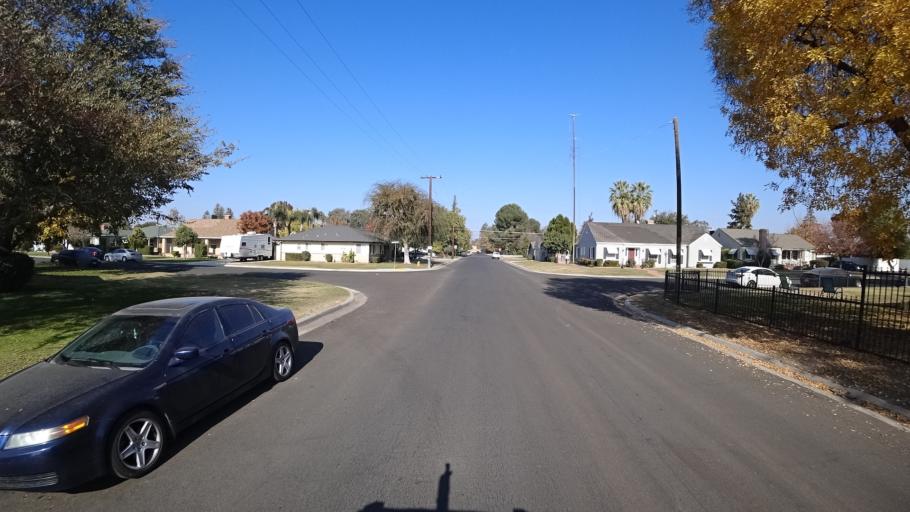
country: US
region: California
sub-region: Kern County
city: Bakersfield
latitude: 35.3493
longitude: -119.0257
